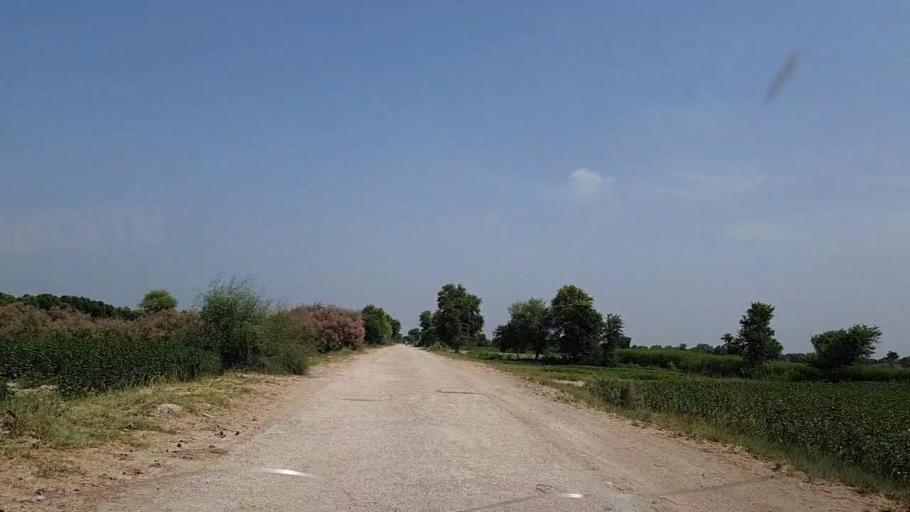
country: PK
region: Sindh
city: Adilpur
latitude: 27.8345
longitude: 69.2857
